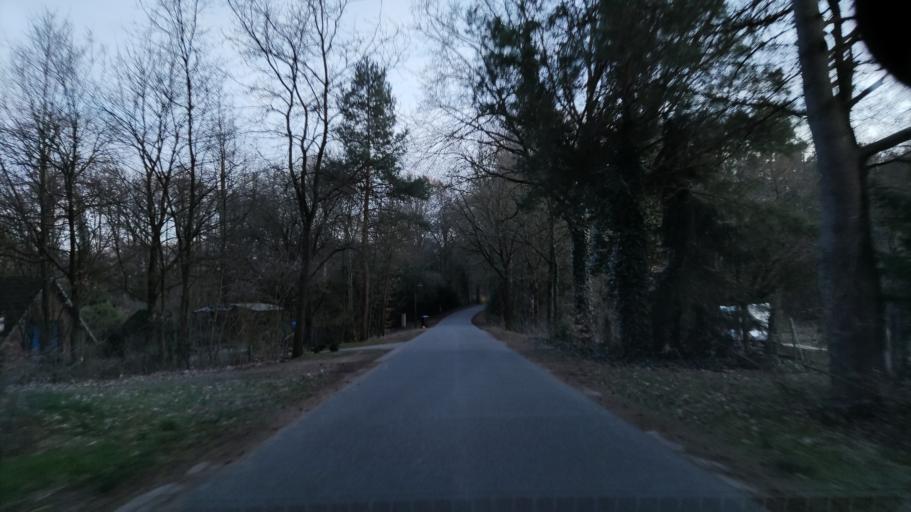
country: DE
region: Lower Saxony
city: Thomasburg
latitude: 53.2039
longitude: 10.6784
